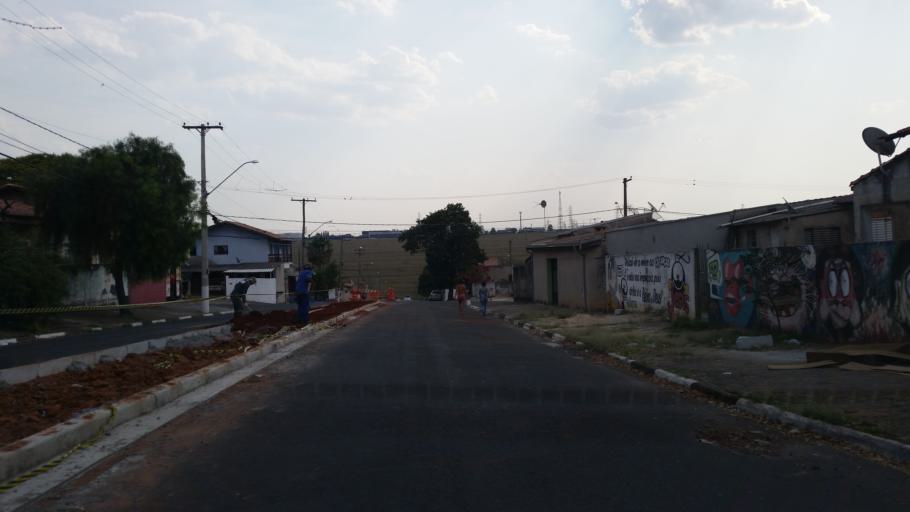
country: BR
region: Sao Paulo
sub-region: Hortolandia
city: Hortolandia
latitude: -22.8896
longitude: -47.1810
